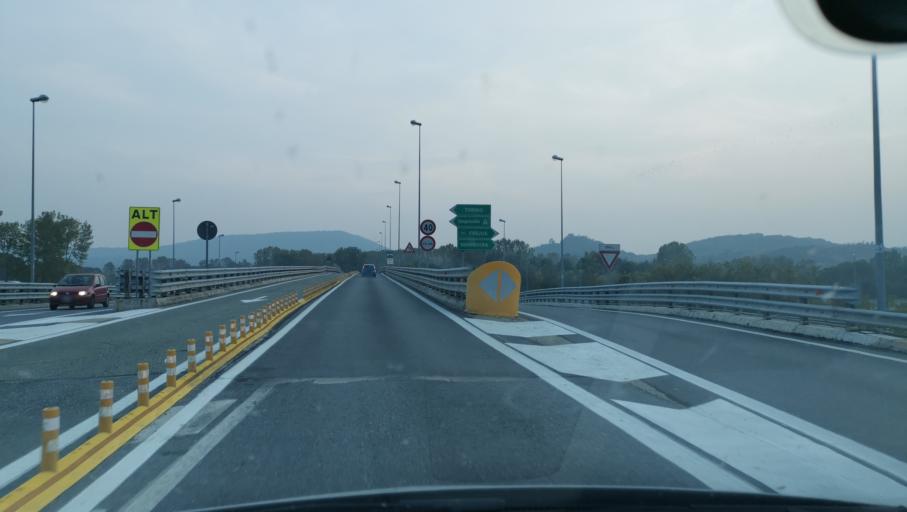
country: IT
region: Piedmont
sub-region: Provincia di Torino
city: Avigliana
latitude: 45.0954
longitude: 7.3984
